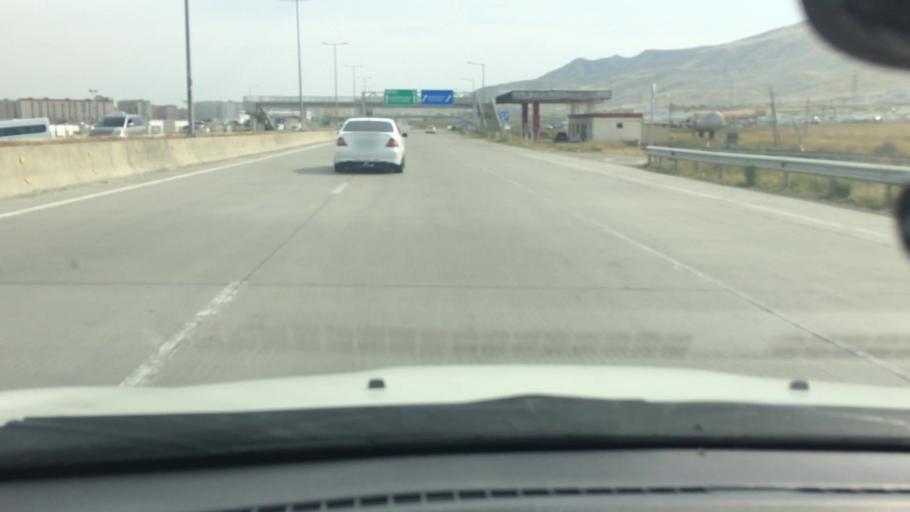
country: GE
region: Kvemo Kartli
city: Rust'avi
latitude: 41.5774
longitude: 44.9555
